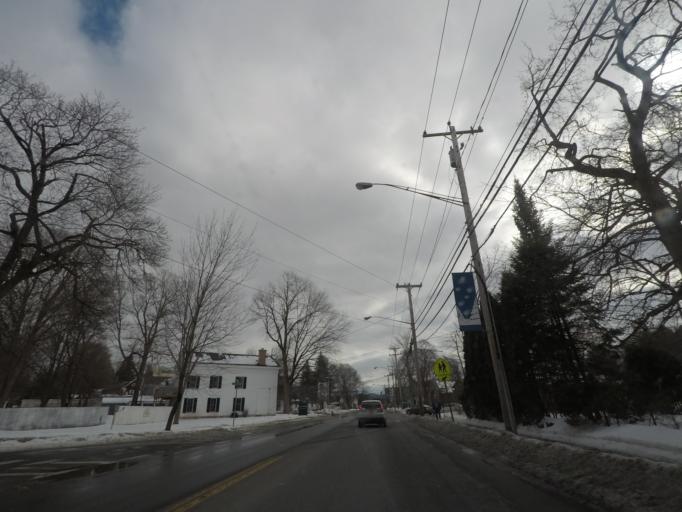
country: US
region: New York
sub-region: Washington County
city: Greenwich
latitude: 43.0922
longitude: -73.5024
